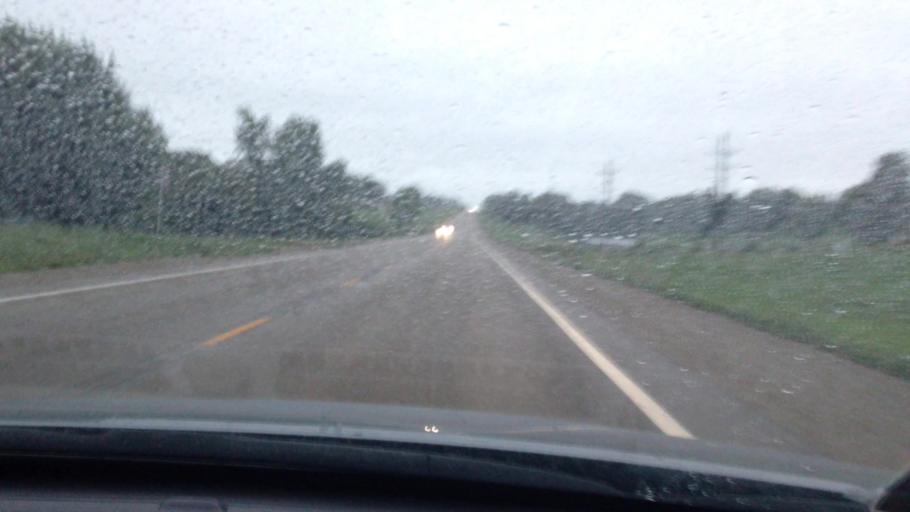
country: US
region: Kansas
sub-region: Brown County
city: Hiawatha
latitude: 39.8284
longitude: -95.5270
